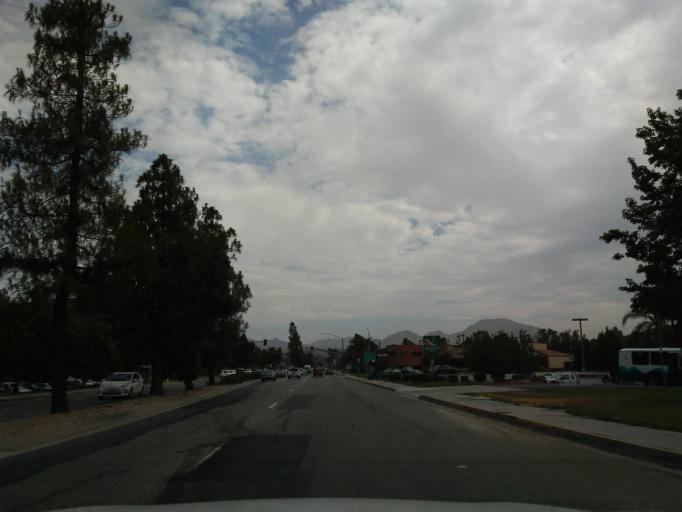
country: US
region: California
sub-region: San Bernardino County
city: Loma Linda
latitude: 34.0700
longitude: -117.2789
